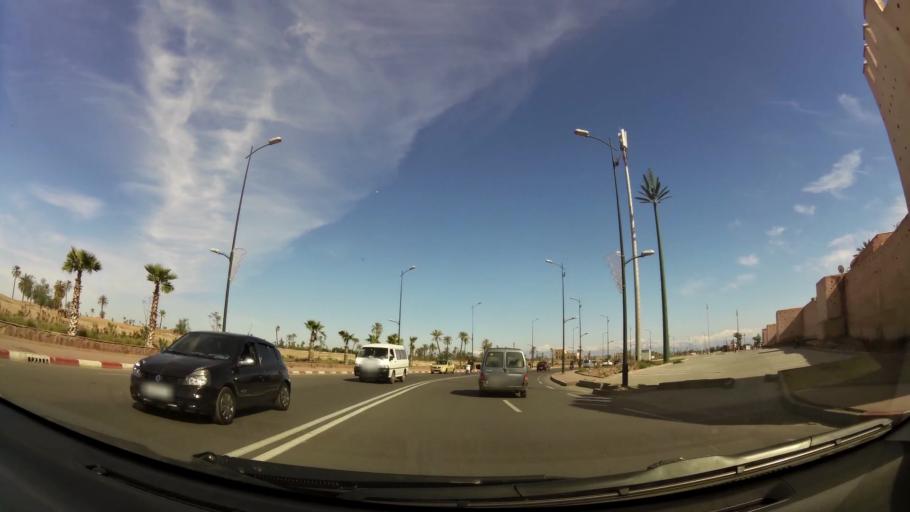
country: MA
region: Marrakech-Tensift-Al Haouz
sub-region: Marrakech
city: Marrakesh
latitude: 31.6321
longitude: -7.9746
